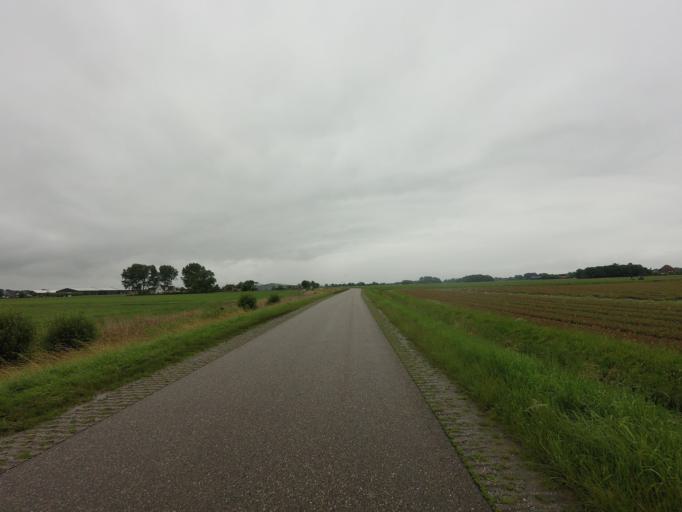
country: NL
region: North Holland
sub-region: Gemeente Schagen
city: Schagen
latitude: 52.7678
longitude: 4.7889
